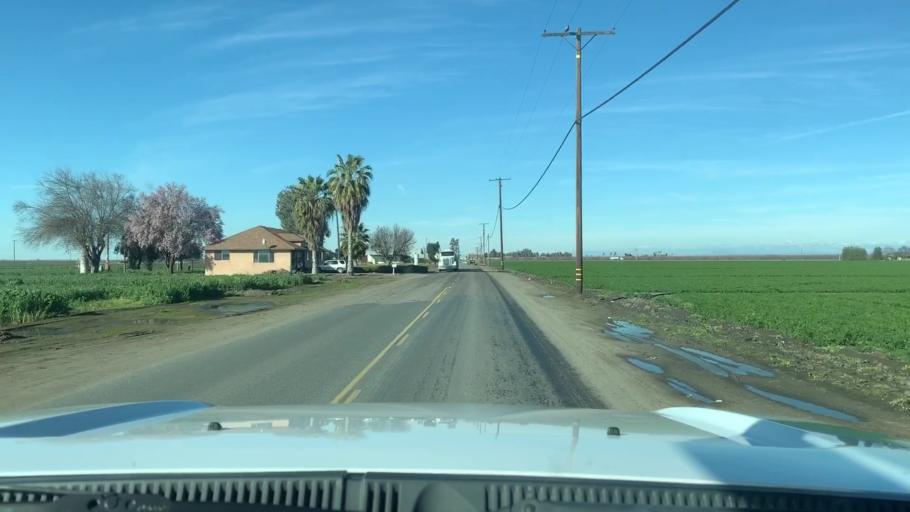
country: US
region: California
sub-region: Kings County
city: Corcoran
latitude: 36.2039
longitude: -119.4930
